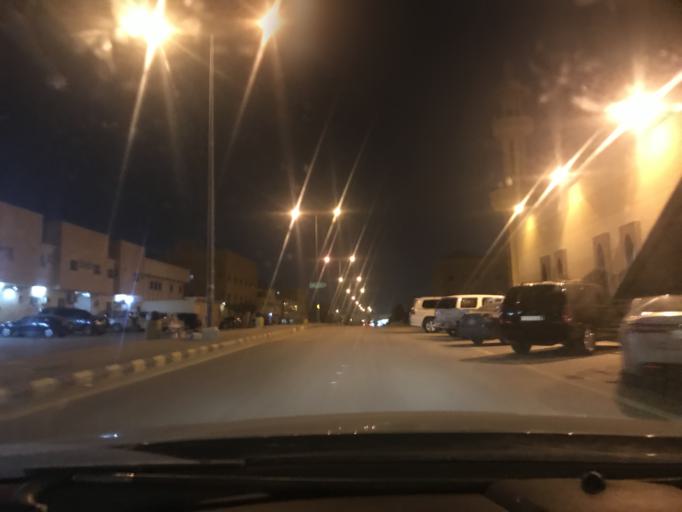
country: SA
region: Ar Riyad
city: Riyadh
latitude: 24.7588
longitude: 46.7468
